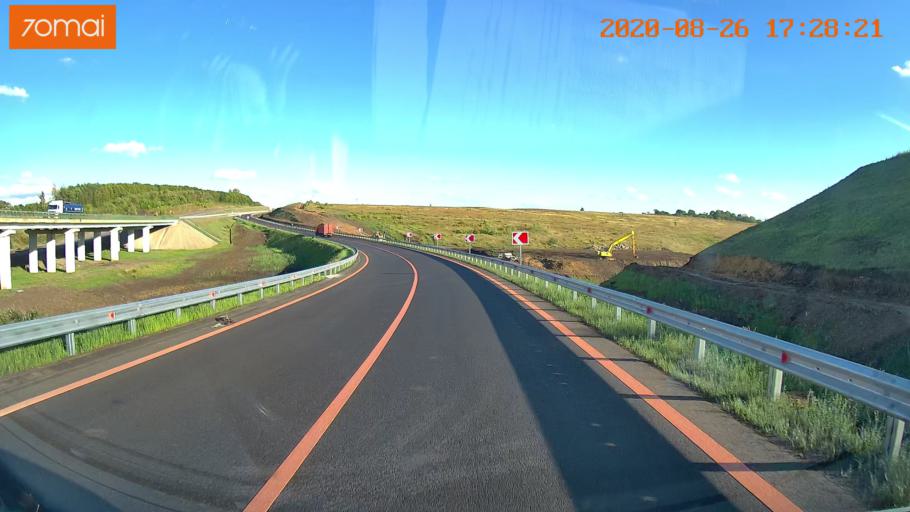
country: RU
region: Tula
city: Kazachka
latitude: 53.4635
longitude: 38.1335
